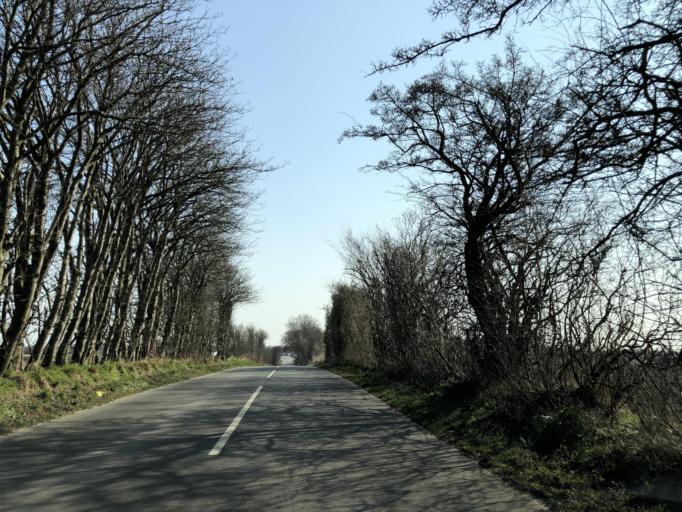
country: DK
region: South Denmark
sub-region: Sonderborg Kommune
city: Nordborg
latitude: 55.0649
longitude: 9.7352
